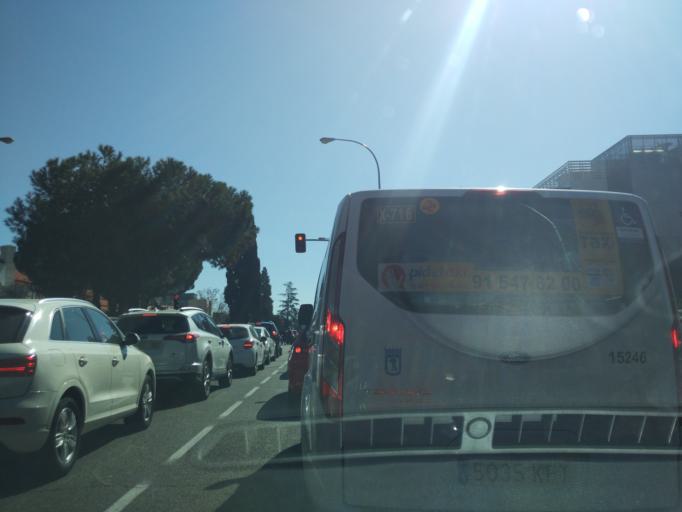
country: ES
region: Madrid
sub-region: Provincia de Madrid
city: Ciudad Lineal
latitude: 40.4504
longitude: -3.6521
